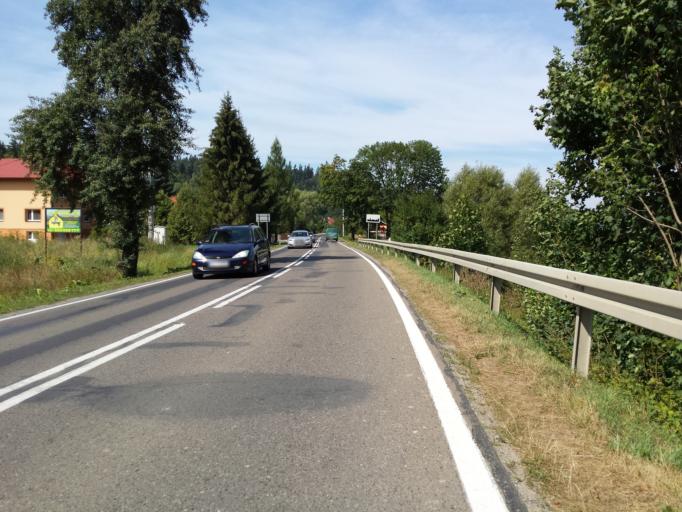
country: PL
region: Subcarpathian Voivodeship
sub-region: Powiat leski
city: Lesko
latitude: 49.4636
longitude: 22.3270
